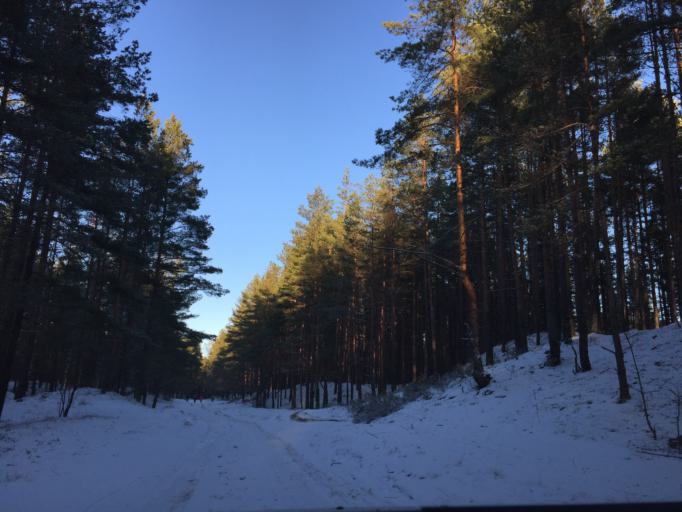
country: LV
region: Kekava
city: Balozi
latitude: 56.8822
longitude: 24.1228
